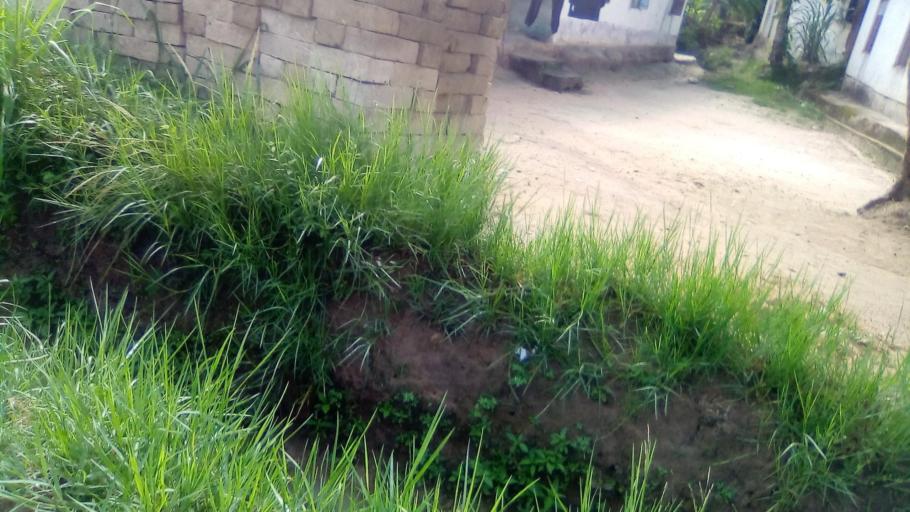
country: SL
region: Southern Province
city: Bo
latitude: 7.9778
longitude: -11.7344
